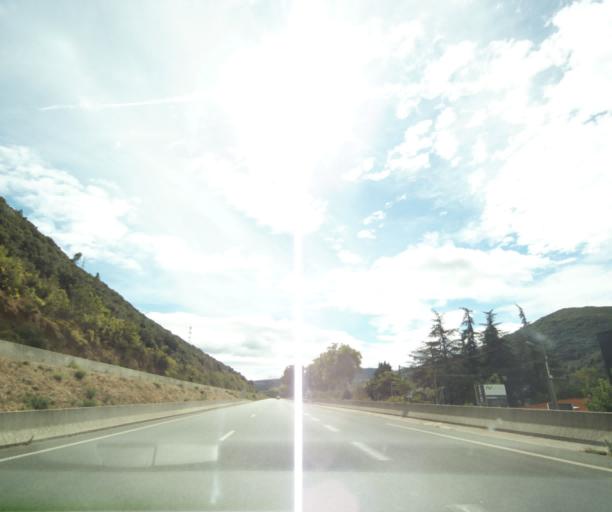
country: FR
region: Languedoc-Roussillon
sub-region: Departement de l'Herault
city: Lodeve
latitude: 43.7196
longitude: 3.3244
